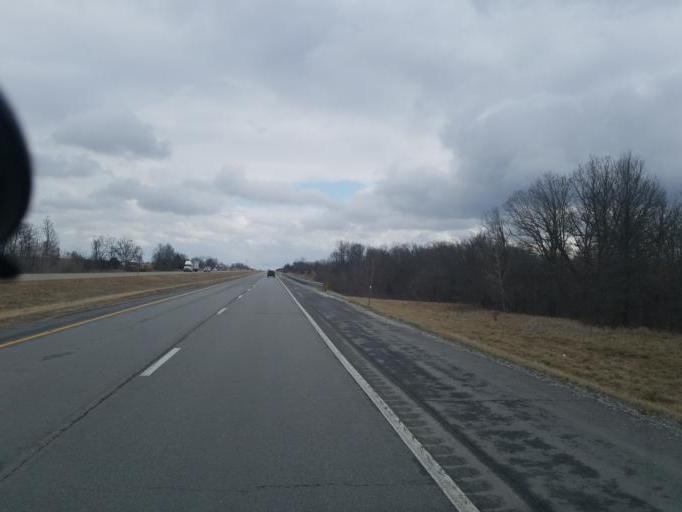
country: US
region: Missouri
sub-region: Randolph County
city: Moberly
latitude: 39.2913
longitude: -92.3717
